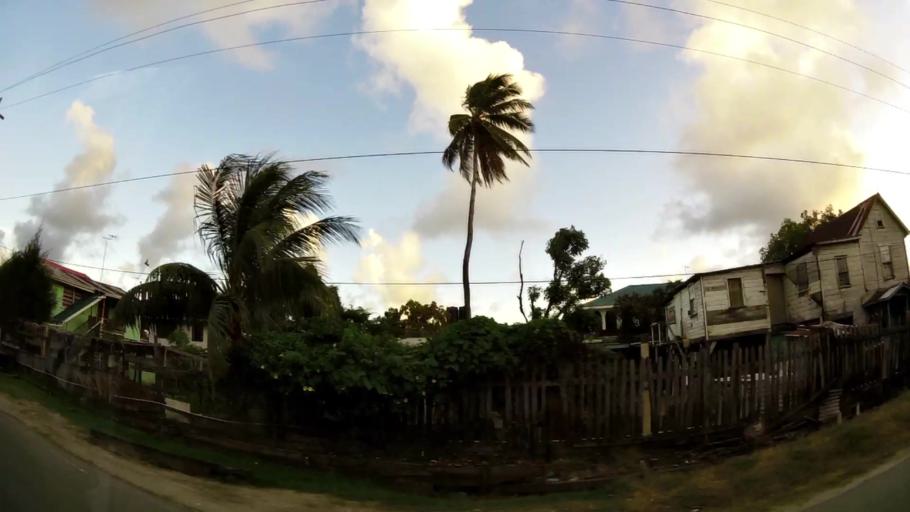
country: GY
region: Demerara-Mahaica
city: Georgetown
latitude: 6.8158
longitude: -58.1072
